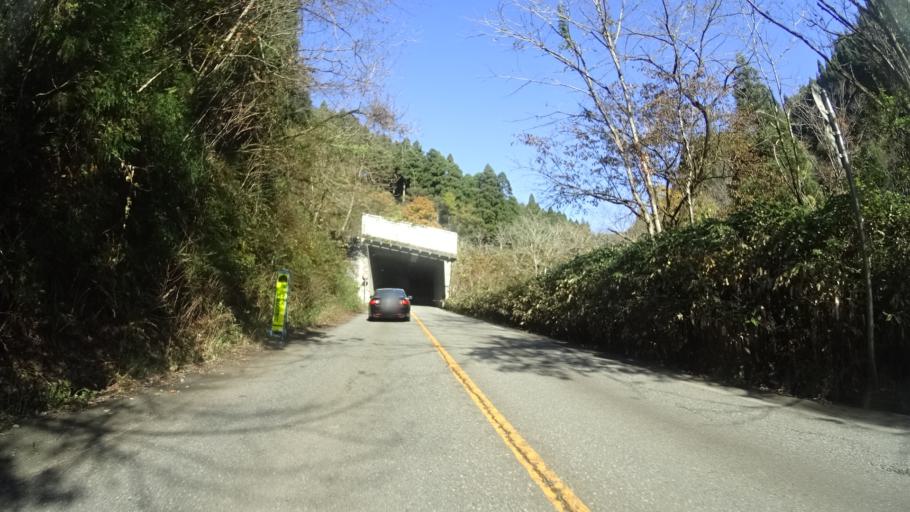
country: JP
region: Ishikawa
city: Tsurugi-asahimachi
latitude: 36.3732
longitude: 136.5813
